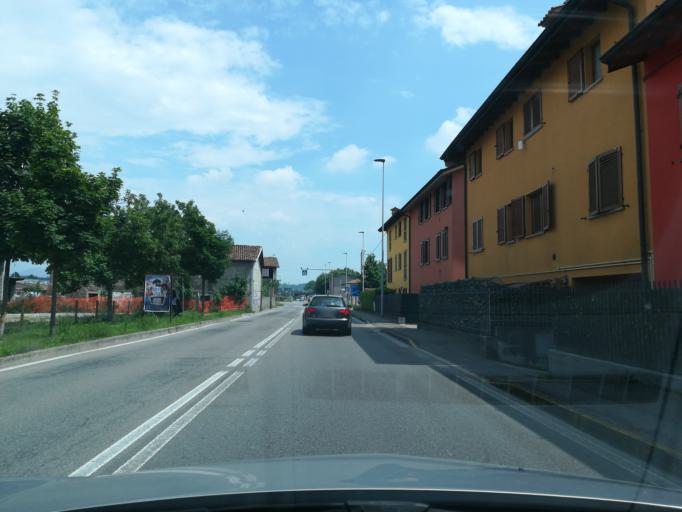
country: IT
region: Lombardy
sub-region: Provincia di Bergamo
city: Seriate
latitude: 45.6785
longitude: 9.7407
